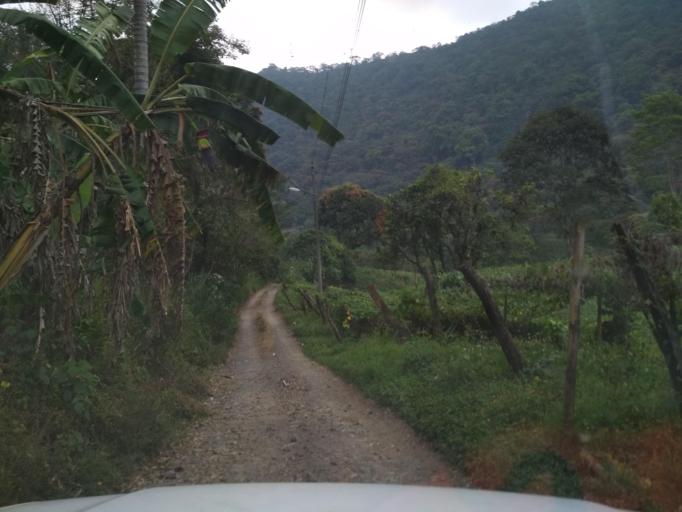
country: MX
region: Veracruz
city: Cuautlapan
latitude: 18.8666
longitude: -97.0139
